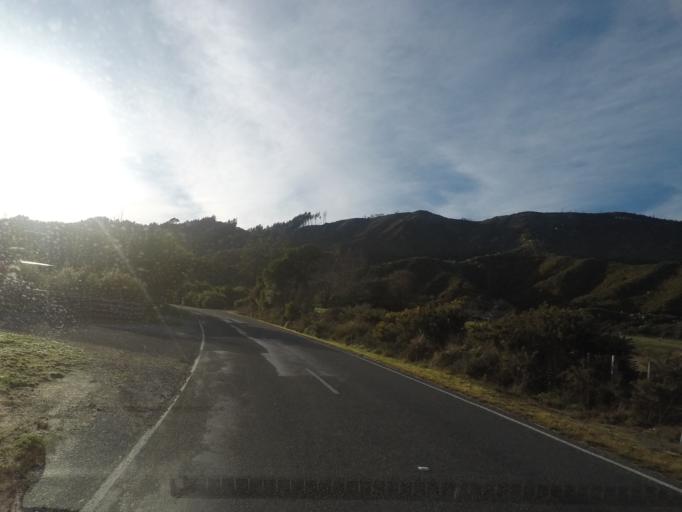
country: NZ
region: Tasman
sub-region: Tasman District
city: Takaka
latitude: -40.8185
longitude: 172.9134
